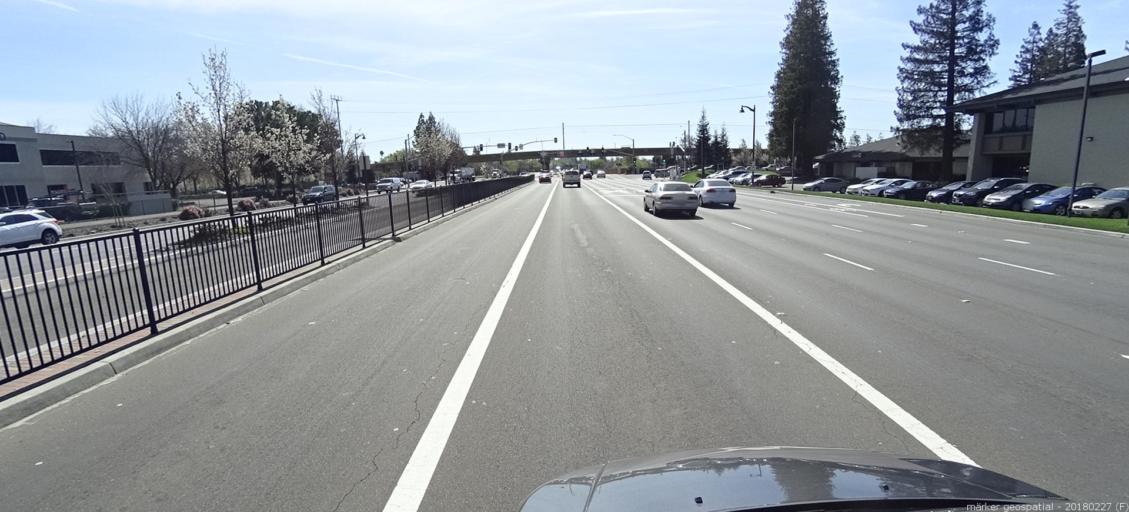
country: US
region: California
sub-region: Sacramento County
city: Rosemont
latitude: 38.5541
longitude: -121.3761
